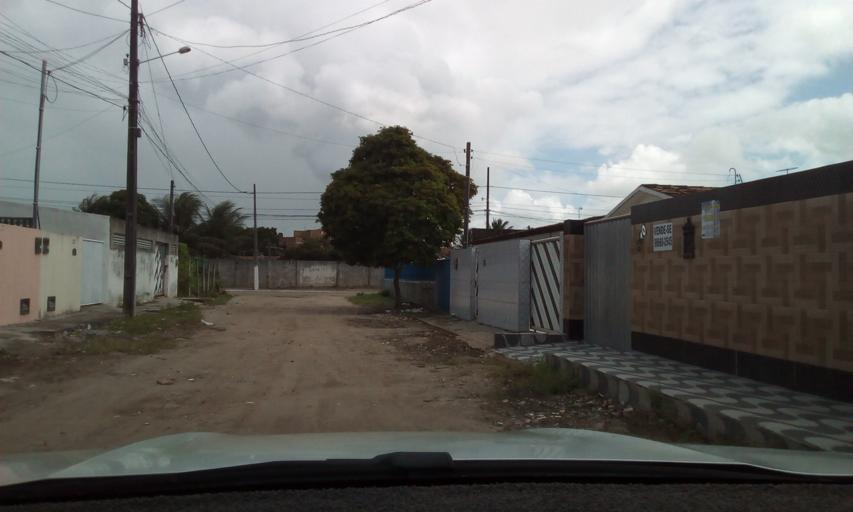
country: BR
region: Paraiba
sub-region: Santa Rita
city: Santa Rita
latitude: -7.1419
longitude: -34.9649
